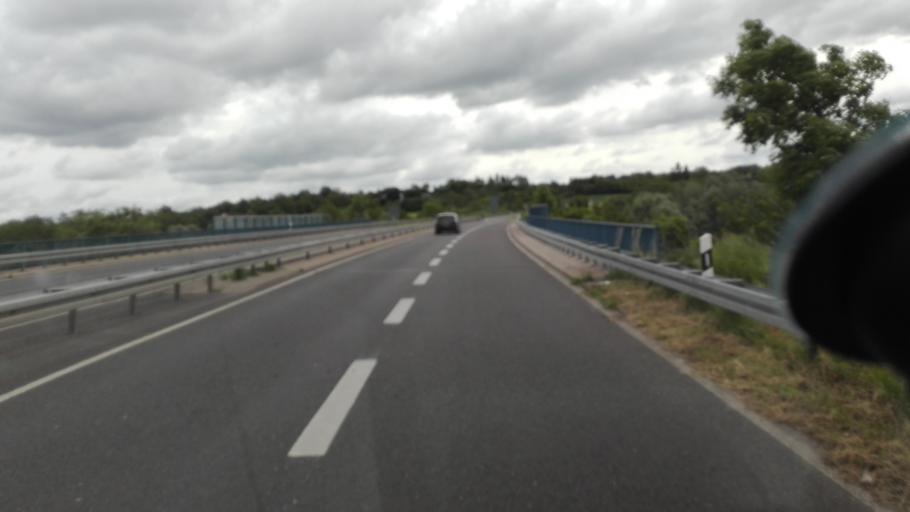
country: DE
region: Baden-Wuerttemberg
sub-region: Karlsruhe Region
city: Bruchsal
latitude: 49.1442
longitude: 8.6036
